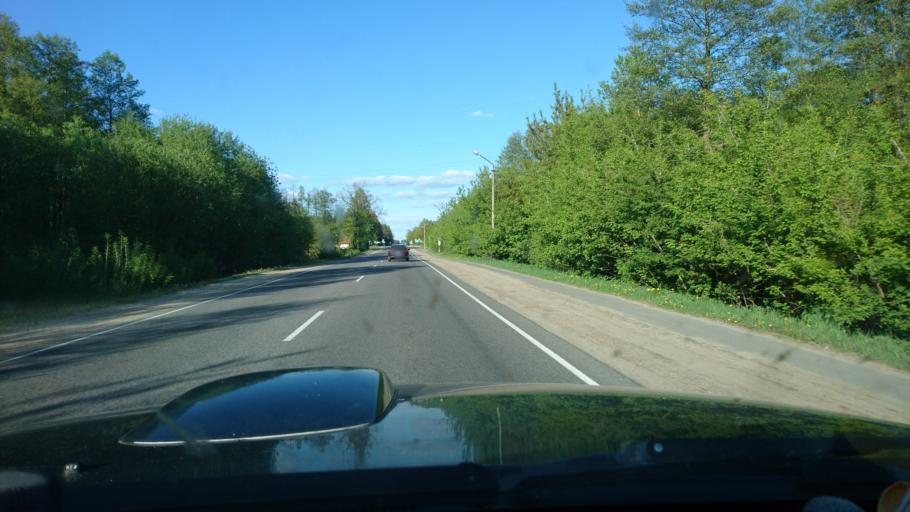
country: BY
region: Brest
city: Byaroza
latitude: 52.5444
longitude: 25.0050
